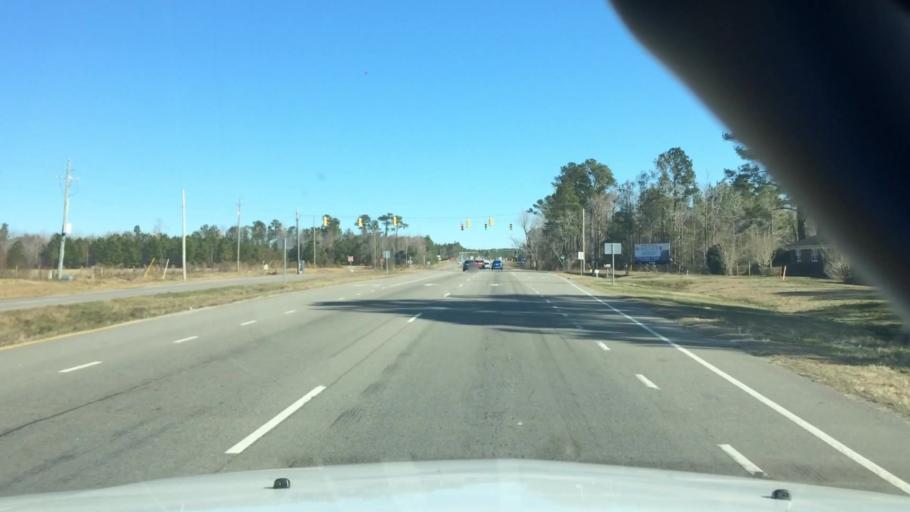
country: US
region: North Carolina
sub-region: Brunswick County
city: Bolivia
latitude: 34.0256
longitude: -78.2616
